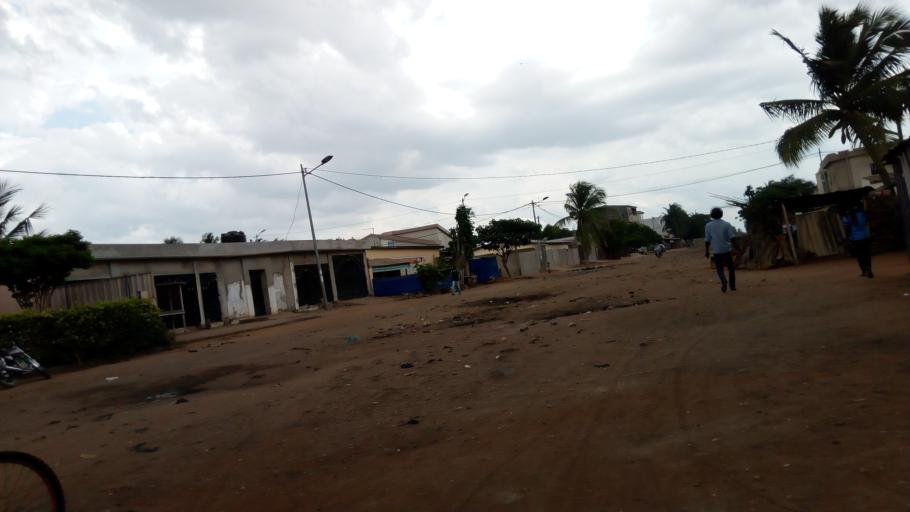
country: TG
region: Maritime
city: Lome
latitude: 6.2161
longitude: 1.1824
